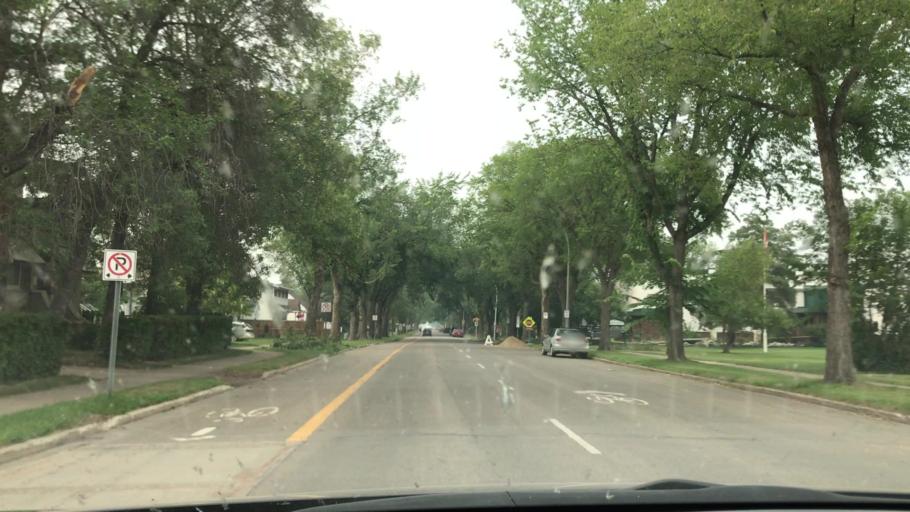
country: CA
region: Alberta
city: Edmonton
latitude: 53.5652
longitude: -113.5412
